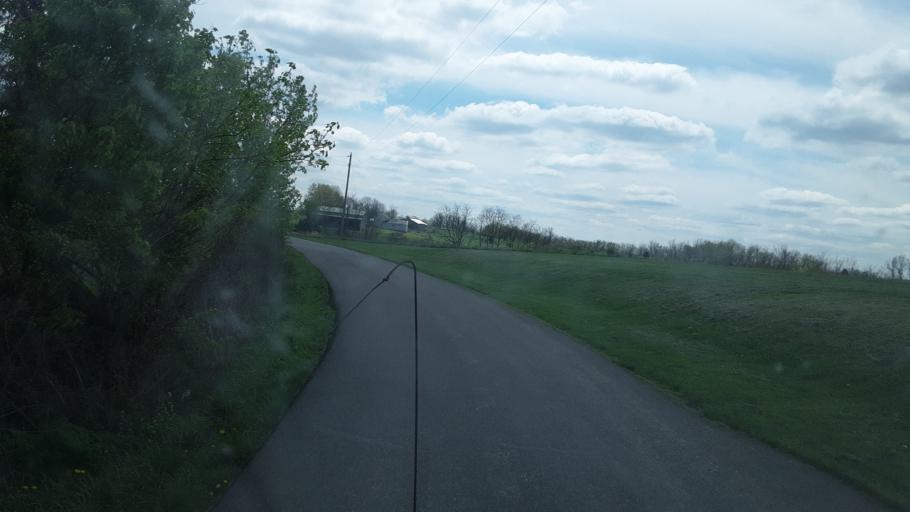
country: US
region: Kentucky
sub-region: Owen County
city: Owenton
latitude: 38.6704
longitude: -84.7831
